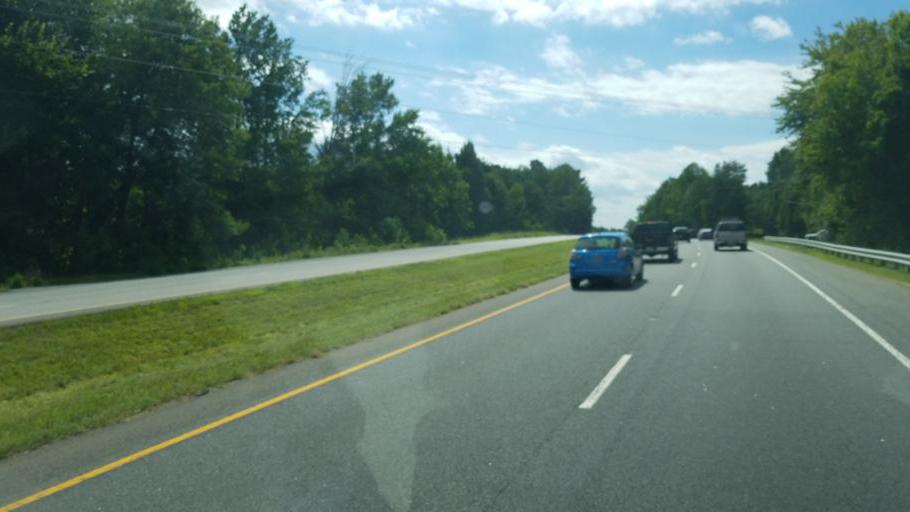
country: US
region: Virginia
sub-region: Stafford County
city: Falmouth
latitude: 38.4190
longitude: -77.6132
